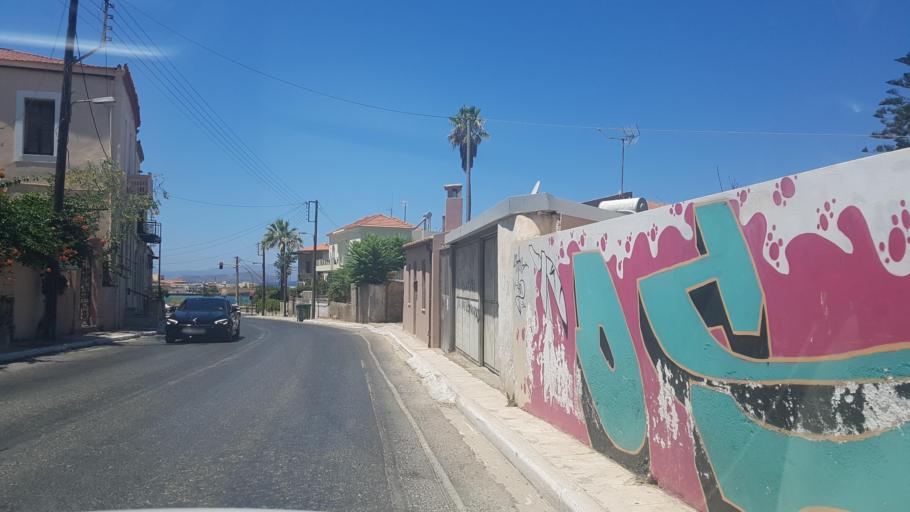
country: GR
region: Crete
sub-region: Nomos Chanias
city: Chania
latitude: 35.5165
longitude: 24.0339
